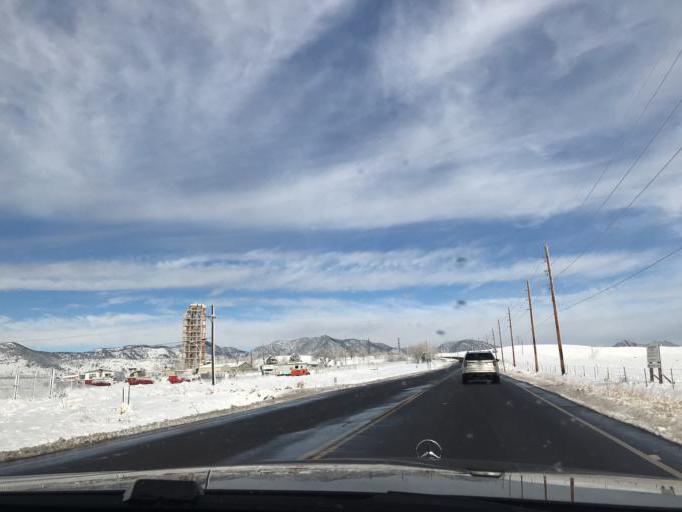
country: US
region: Colorado
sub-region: Boulder County
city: Superior
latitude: 39.8595
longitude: -105.1936
